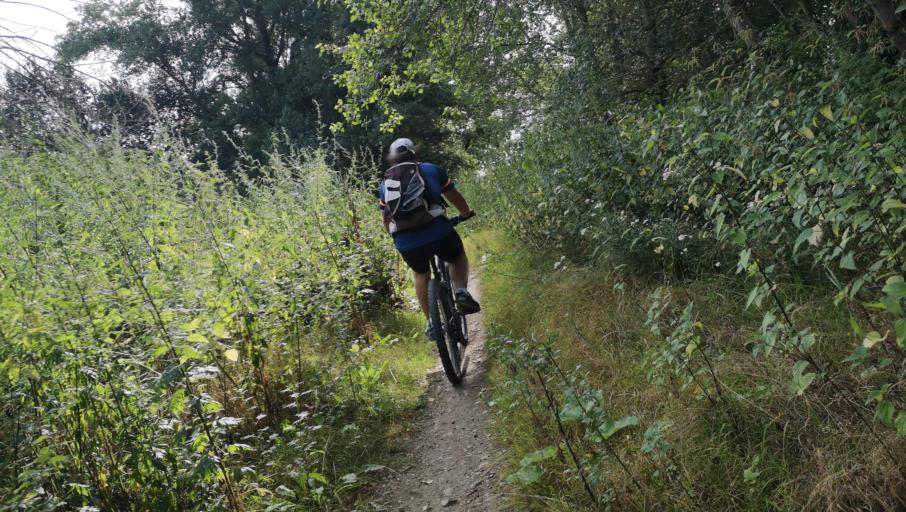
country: FR
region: Centre
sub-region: Departement du Loiret
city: Darvoy
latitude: 47.8733
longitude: 2.0906
